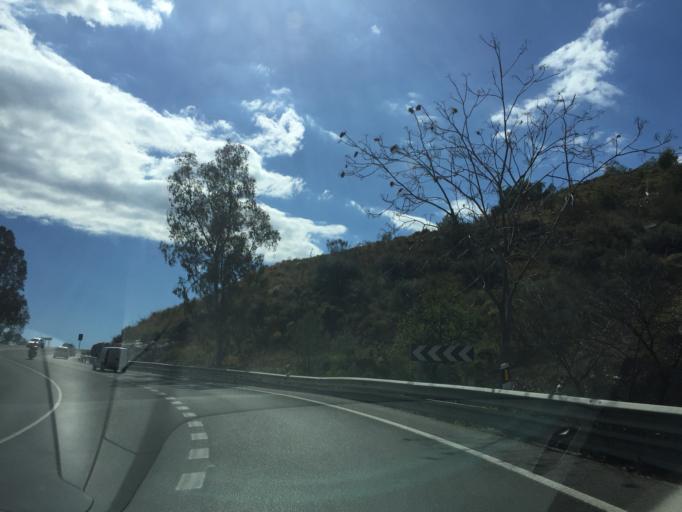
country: ES
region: Andalusia
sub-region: Provincia de Granada
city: Almunecar
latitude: 36.7408
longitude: -3.7063
